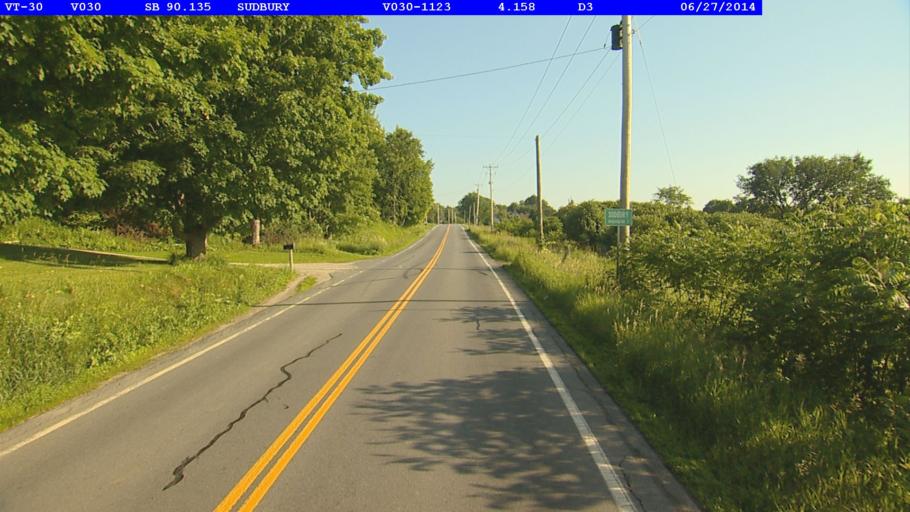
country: US
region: Vermont
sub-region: Rutland County
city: Brandon
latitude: 43.8073
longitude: -73.2011
